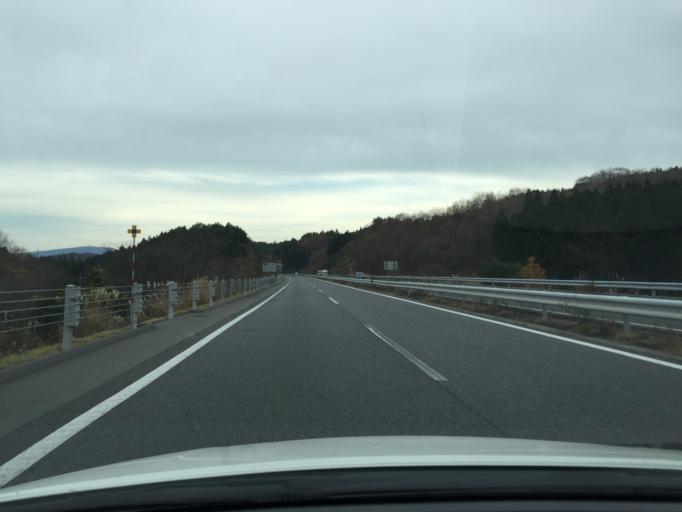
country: JP
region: Fukushima
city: Iwaki
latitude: 37.1892
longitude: 140.7082
